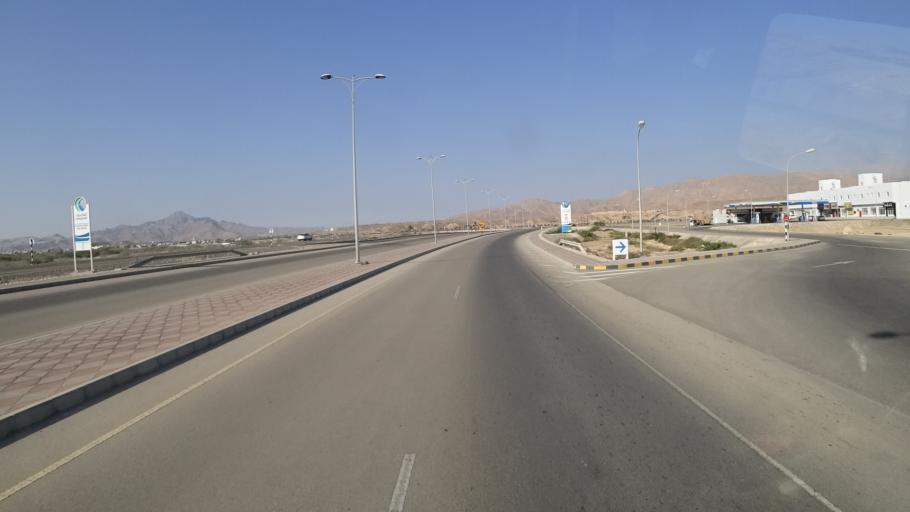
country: OM
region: Ash Sharqiyah
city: Sur
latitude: 22.5830
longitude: 59.4736
